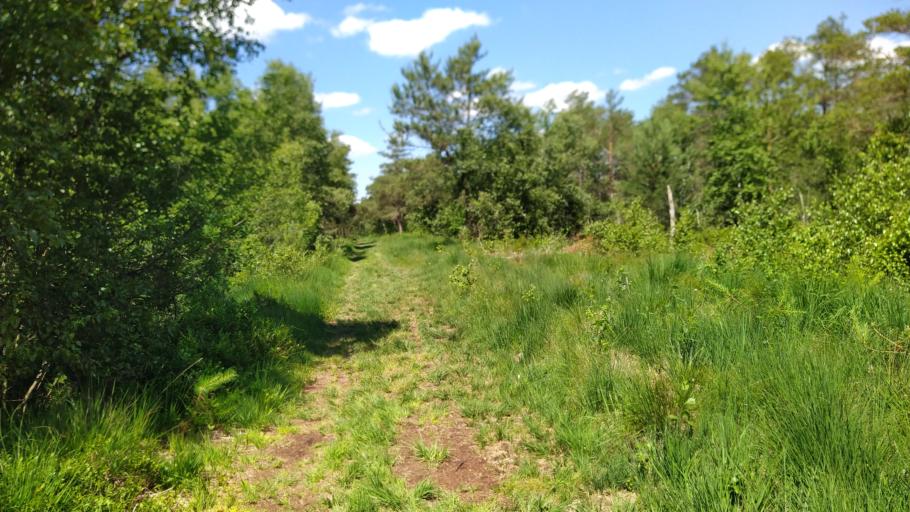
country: DE
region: Lower Saxony
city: Oldendorf
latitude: 53.5553
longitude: 9.2574
